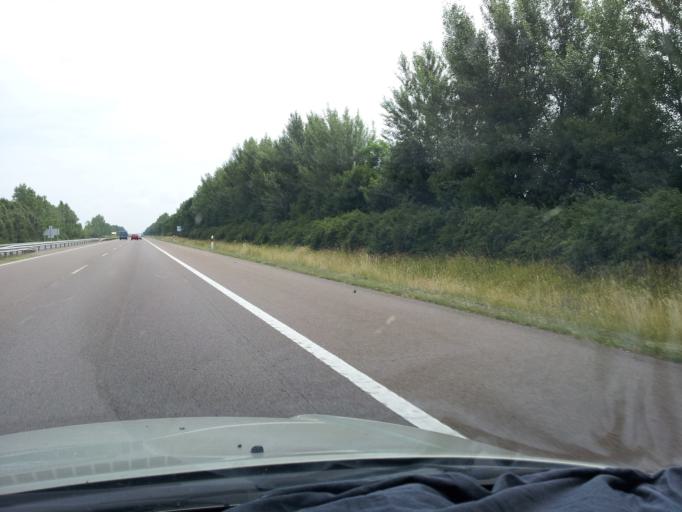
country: HU
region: Borsod-Abauj-Zemplen
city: Mezokovesd
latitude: 47.7815
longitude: 20.5977
